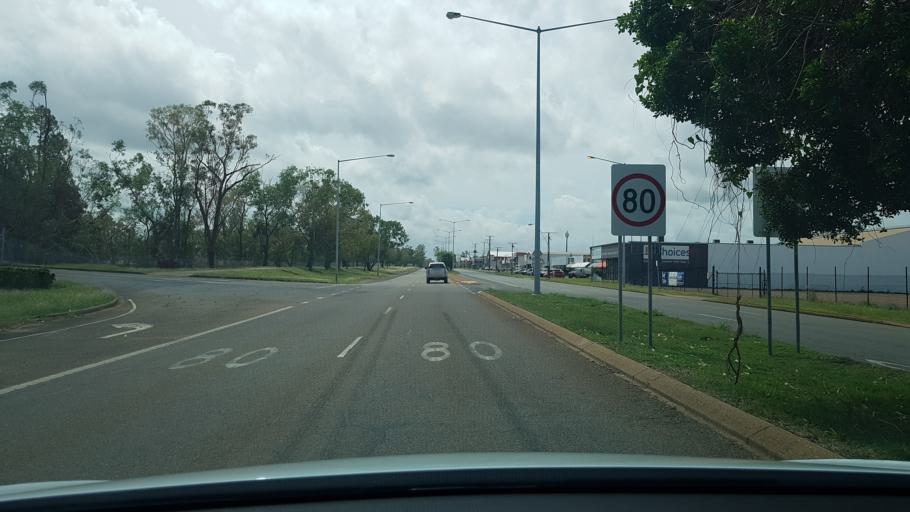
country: AU
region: Northern Territory
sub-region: Darwin
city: Ludmilla
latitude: -12.4252
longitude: 130.8723
